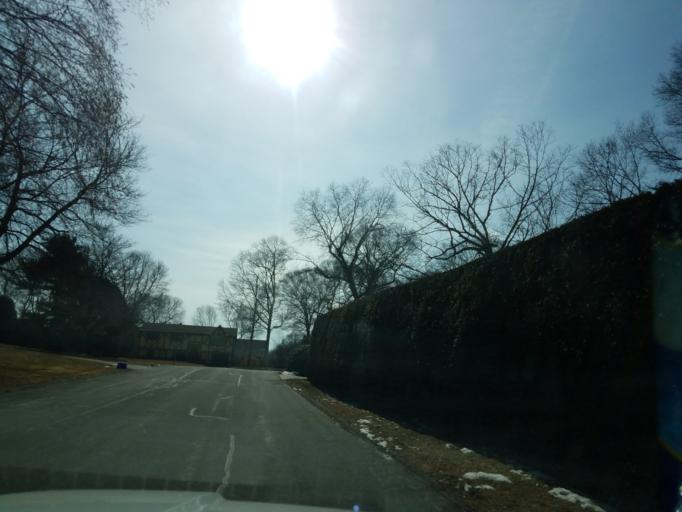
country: US
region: Connecticut
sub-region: New London County
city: Pawcatuck
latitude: 41.3968
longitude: -71.8537
